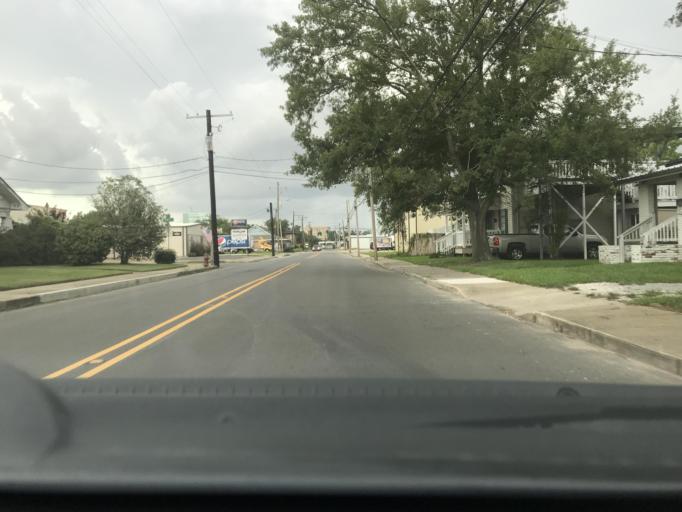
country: US
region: Louisiana
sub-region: Calcasieu Parish
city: Lake Charles
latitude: 30.2178
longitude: -93.2160
